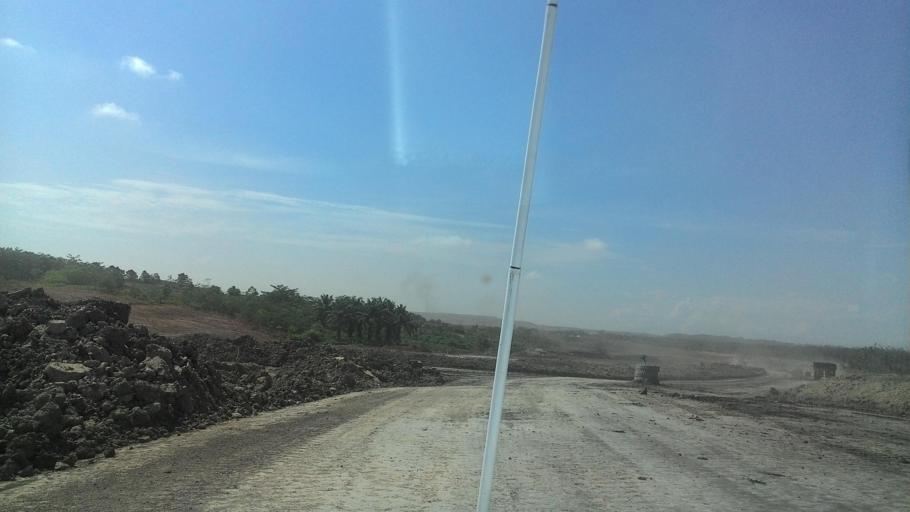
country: ID
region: South Kalimantan
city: Tanta
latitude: -2.1841
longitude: 115.4706
